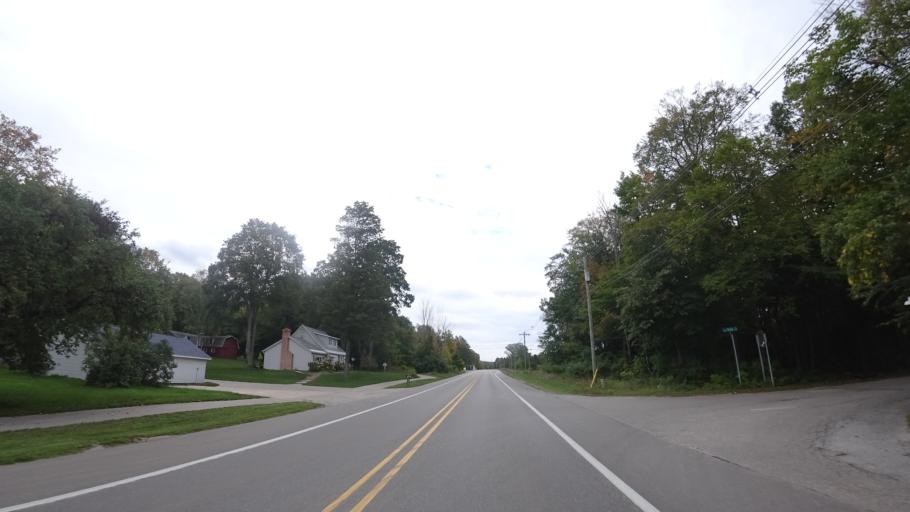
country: US
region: Michigan
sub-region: Emmet County
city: Harbor Springs
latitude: 45.4315
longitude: -84.9467
